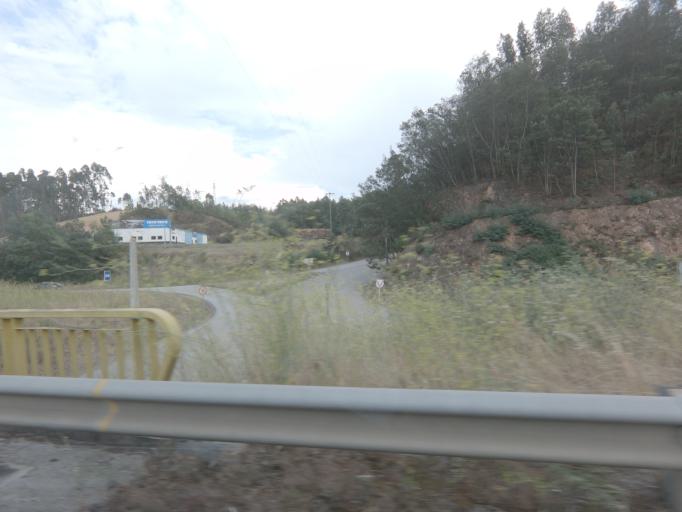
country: PT
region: Coimbra
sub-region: Penacova
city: Penacova
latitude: 40.2937
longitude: -8.2549
